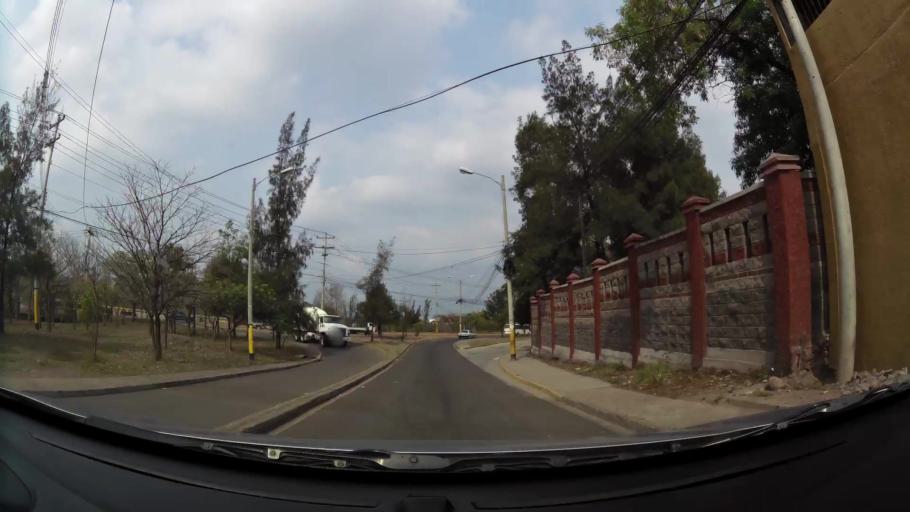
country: HN
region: Francisco Morazan
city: Tegucigalpa
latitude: 14.0824
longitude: -87.1606
